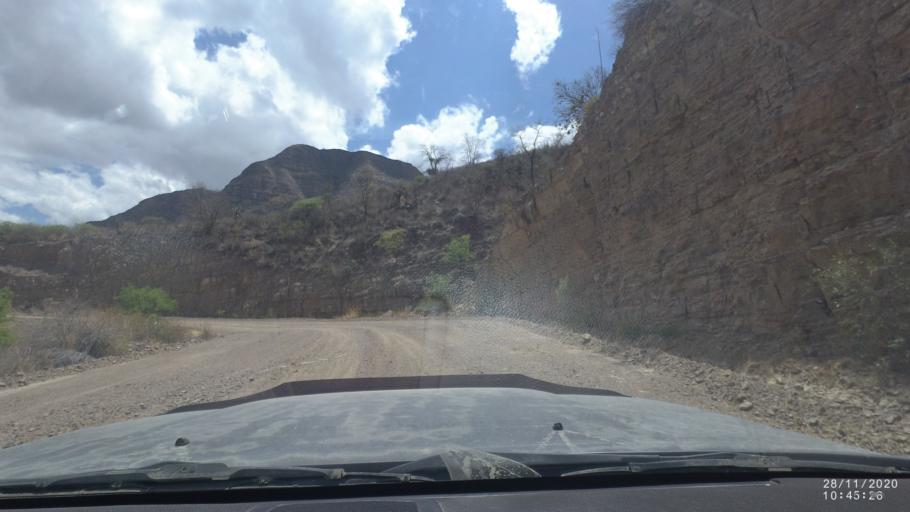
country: BO
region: Cochabamba
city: Capinota
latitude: -17.7874
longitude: -66.1301
